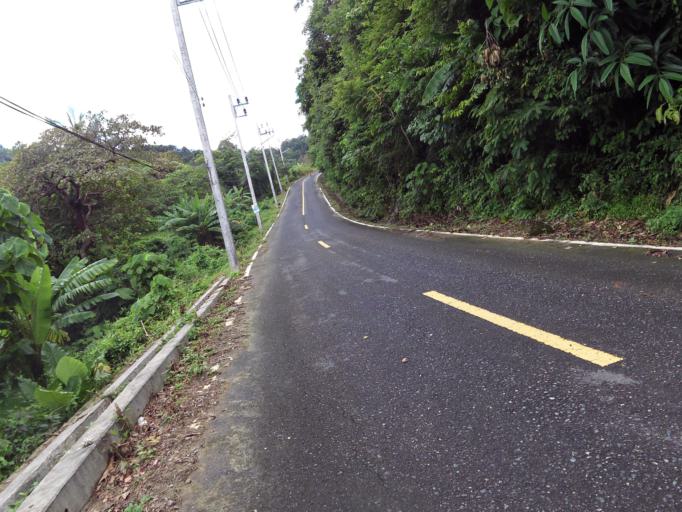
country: TH
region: Phuket
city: Ban Karon
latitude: 7.8577
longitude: 98.2968
